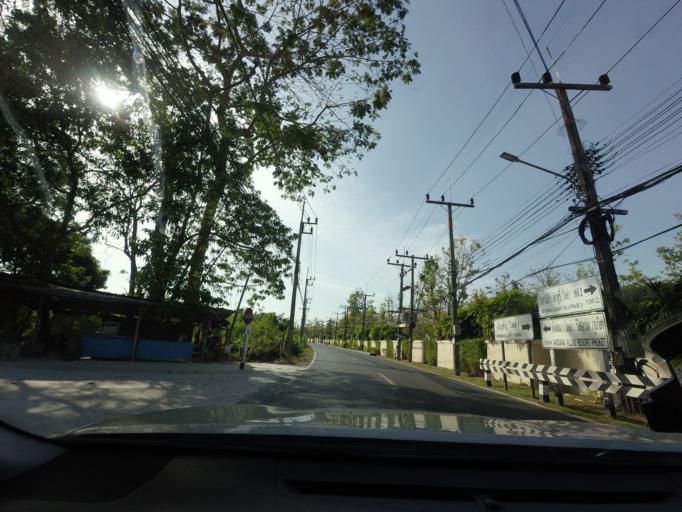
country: TH
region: Phuket
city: Thalang
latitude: 8.0189
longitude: 98.3037
